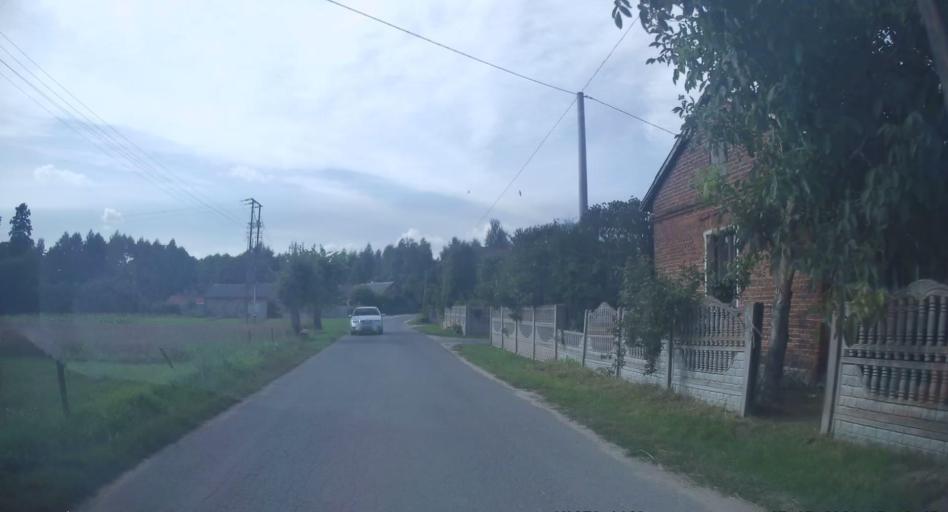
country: PL
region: Lodz Voivodeship
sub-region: Powiat rawski
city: Rawa Mazowiecka
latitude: 51.6943
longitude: 20.2524
